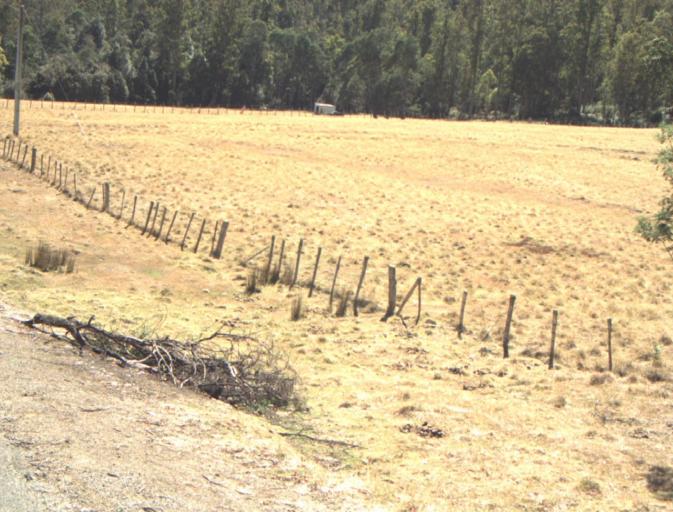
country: AU
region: Tasmania
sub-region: Dorset
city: Scottsdale
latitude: -41.2897
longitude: 147.3408
